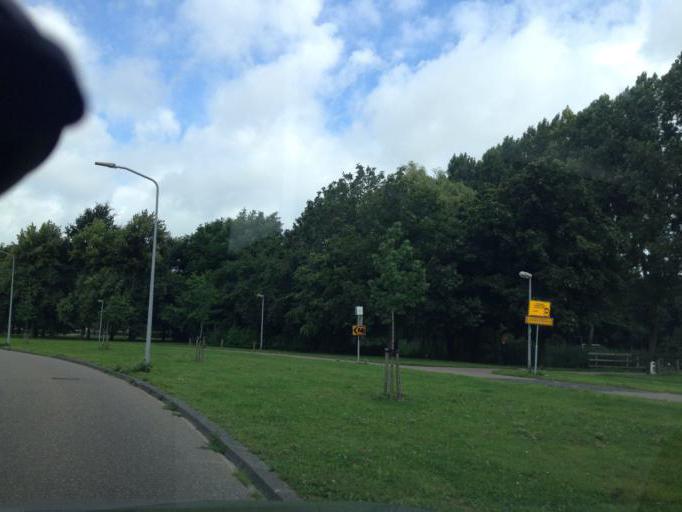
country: NL
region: Flevoland
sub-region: Gemeente Almere
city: Almere Stad
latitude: 52.3726
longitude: 5.1915
